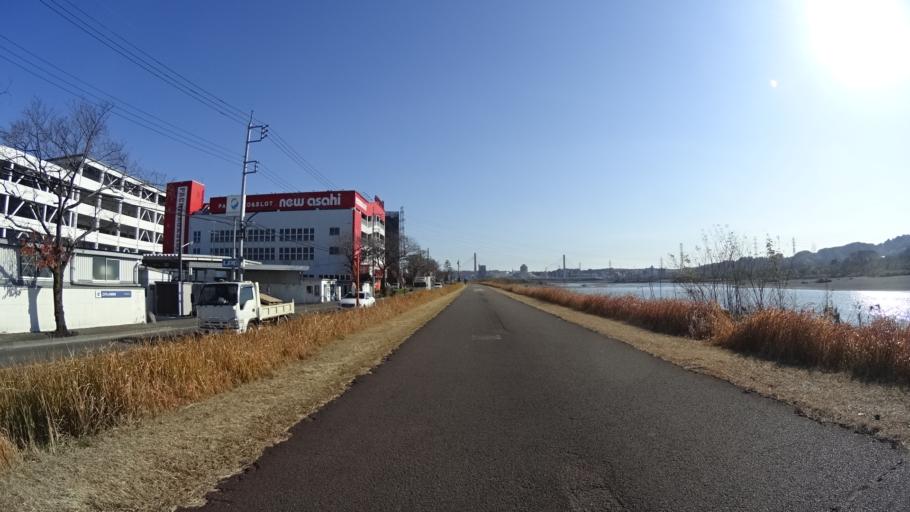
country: JP
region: Tokyo
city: Hino
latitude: 35.6680
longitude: 139.4338
